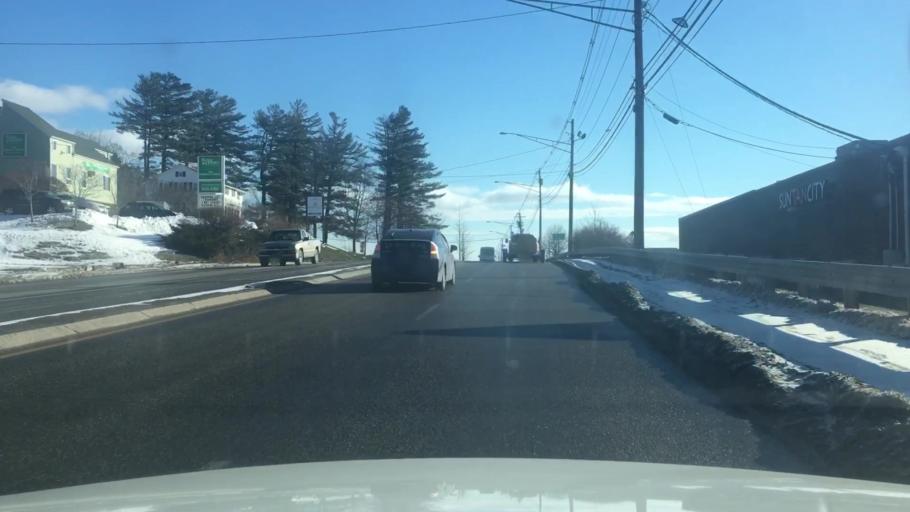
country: US
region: Maine
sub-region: Kennebec County
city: Augusta
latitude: 44.3129
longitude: -69.7943
